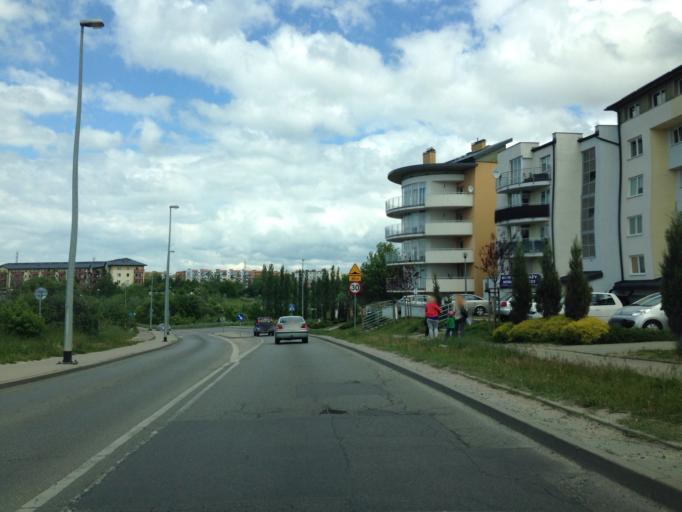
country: PL
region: Pomeranian Voivodeship
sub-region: Powiat gdanski
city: Kowale
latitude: 54.3318
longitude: 18.6010
